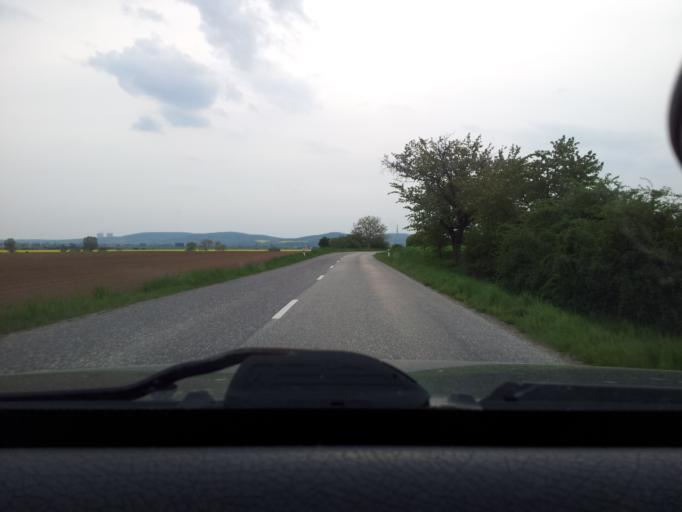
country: SK
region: Nitriansky
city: Tlmace
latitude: 48.2865
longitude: 18.5909
